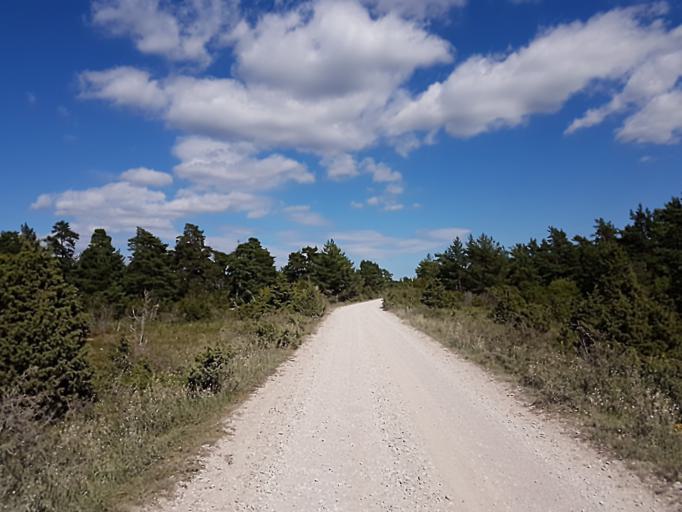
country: SE
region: Gotland
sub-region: Gotland
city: Visby
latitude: 57.6060
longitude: 18.3547
